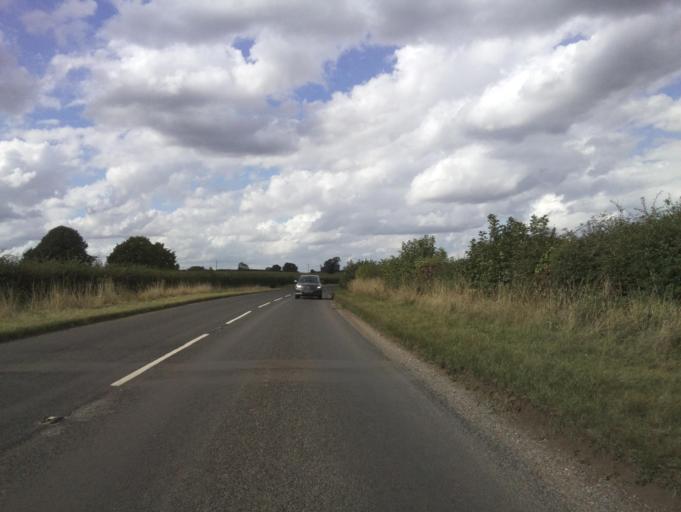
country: GB
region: England
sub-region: North Yorkshire
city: Ripon
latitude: 54.1649
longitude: -1.5485
